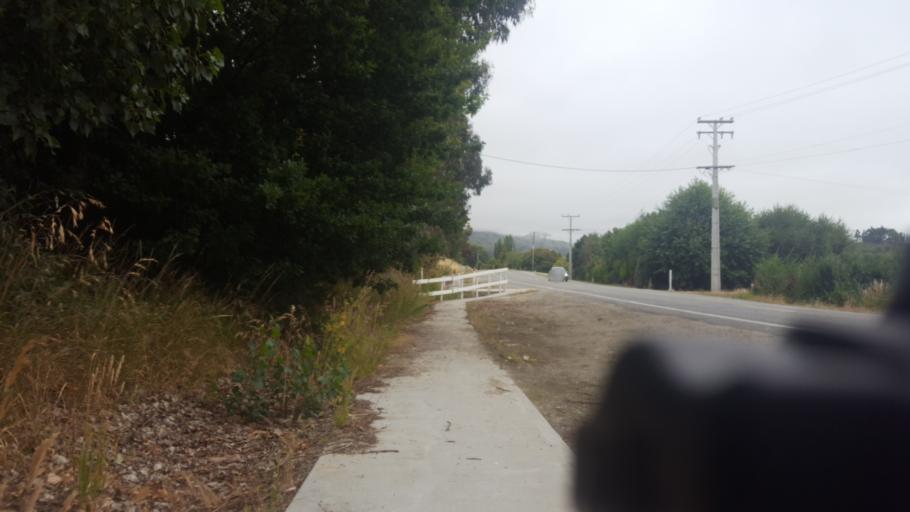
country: NZ
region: Otago
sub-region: Queenstown-Lakes District
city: Kingston
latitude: -45.5322
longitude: 169.2994
